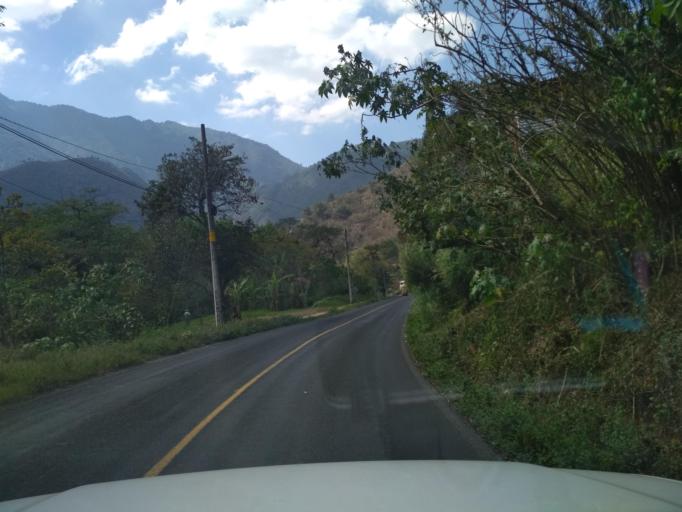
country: MX
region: Veracruz
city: Jalapilla
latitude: 18.7909
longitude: -97.0961
